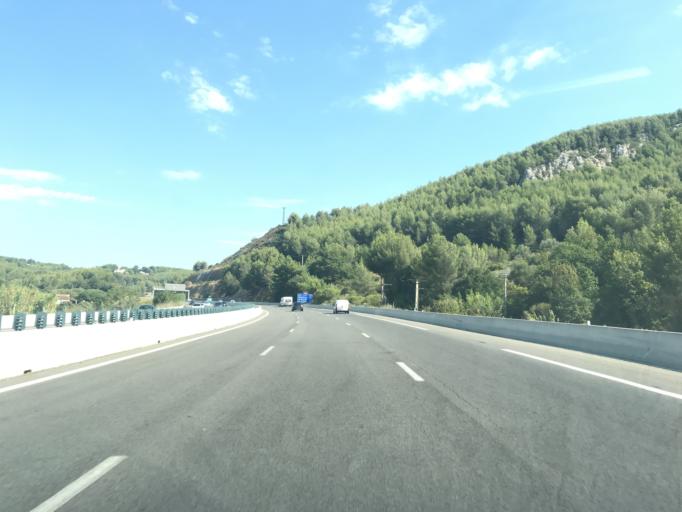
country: FR
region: Provence-Alpes-Cote d'Azur
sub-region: Departement du Var
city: Bandol
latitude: 43.1585
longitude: 5.7672
